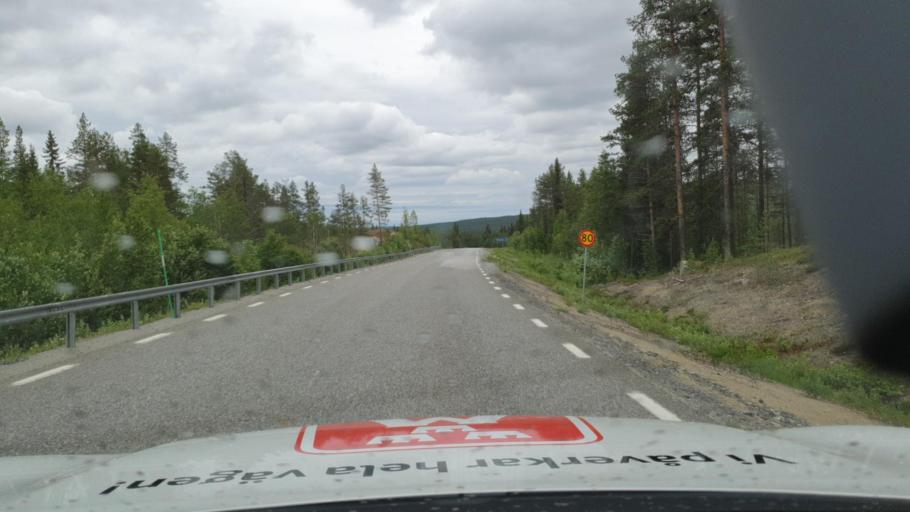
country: SE
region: Vaesterbotten
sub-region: Lycksele Kommun
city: Lycksele
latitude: 64.2401
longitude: 18.2278
